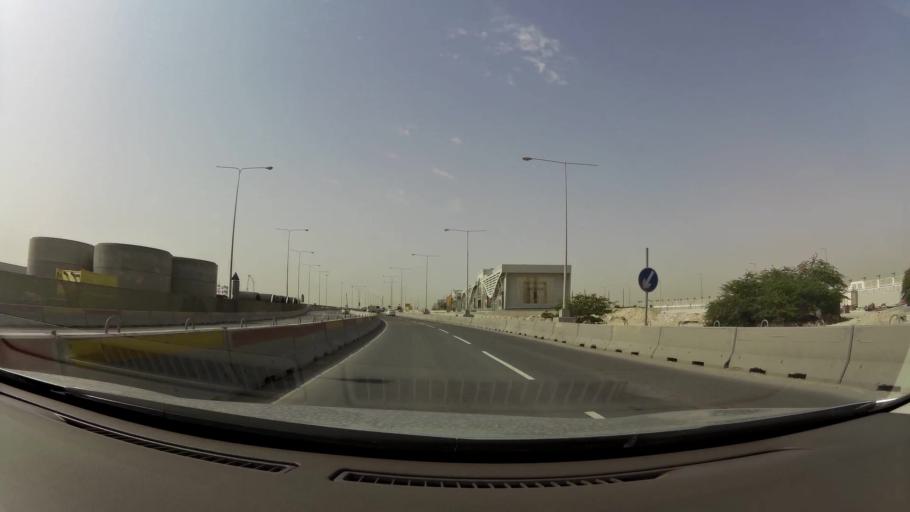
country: QA
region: Baladiyat ad Dawhah
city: Doha
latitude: 25.2258
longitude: 51.5084
